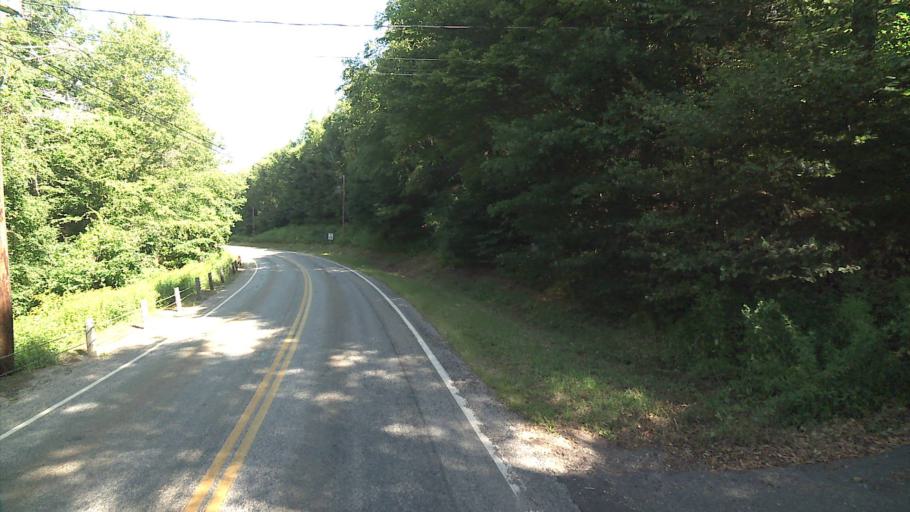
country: US
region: Connecticut
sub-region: Litchfield County
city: Plymouth
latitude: 41.7069
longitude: -73.0547
